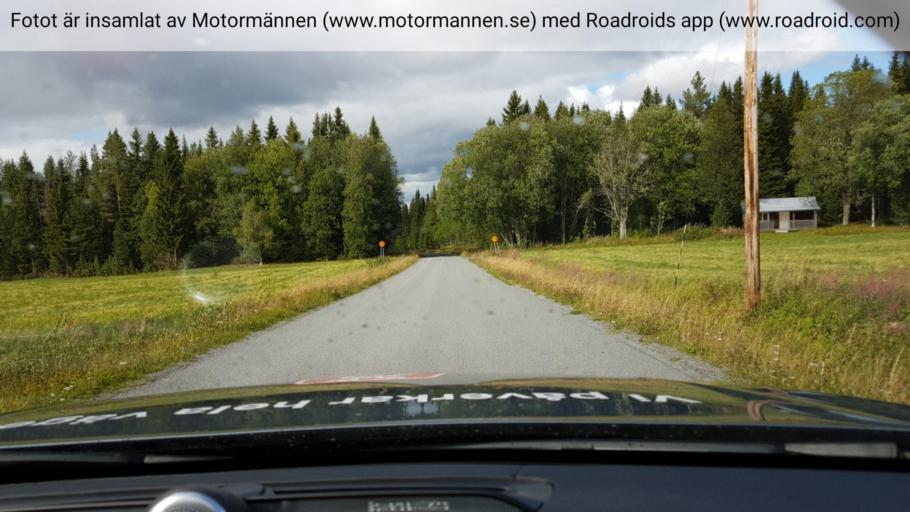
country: SE
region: Jaemtland
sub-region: OEstersunds Kommun
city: Lit
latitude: 63.6442
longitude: 14.9543
